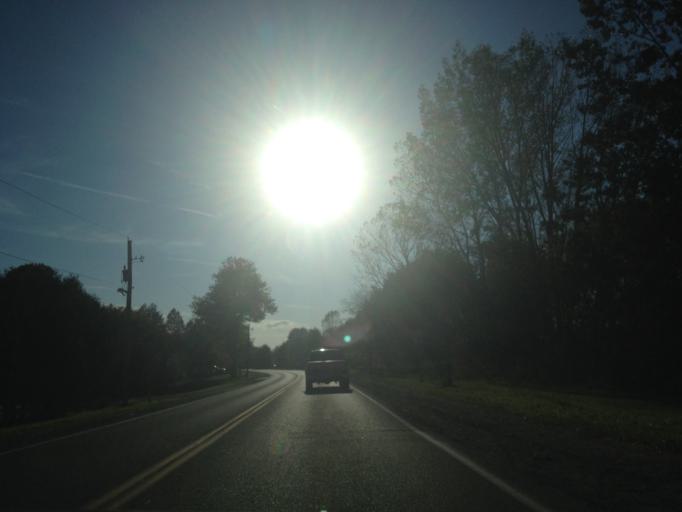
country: CA
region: Ontario
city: Delaware
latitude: 42.6097
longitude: -81.5975
